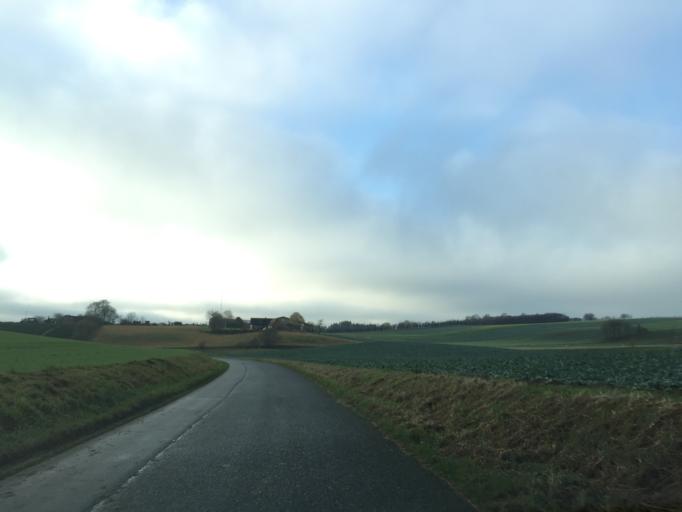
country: DK
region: Central Jutland
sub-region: Skanderborg Kommune
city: Ry
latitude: 56.1682
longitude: 9.7779
